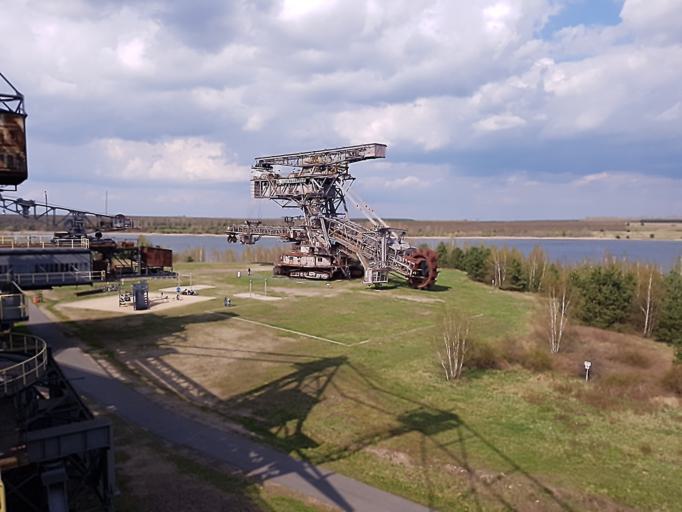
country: DE
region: Saxony-Anhalt
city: Grafenhainichen
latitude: 51.7587
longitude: 12.4493
